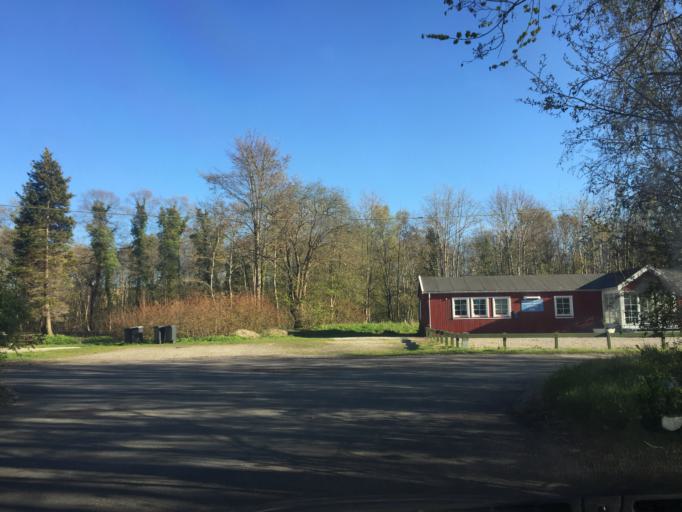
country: DK
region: Capital Region
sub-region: Halsnaes Kommune
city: Frederiksvaerk
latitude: 55.9747
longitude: 12.0108
